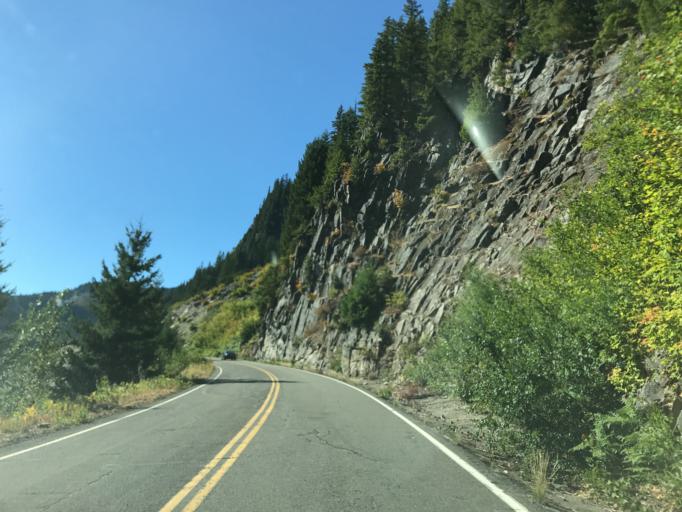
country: US
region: Washington
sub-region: Pierce County
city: Buckley
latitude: 46.7688
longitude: -121.6764
